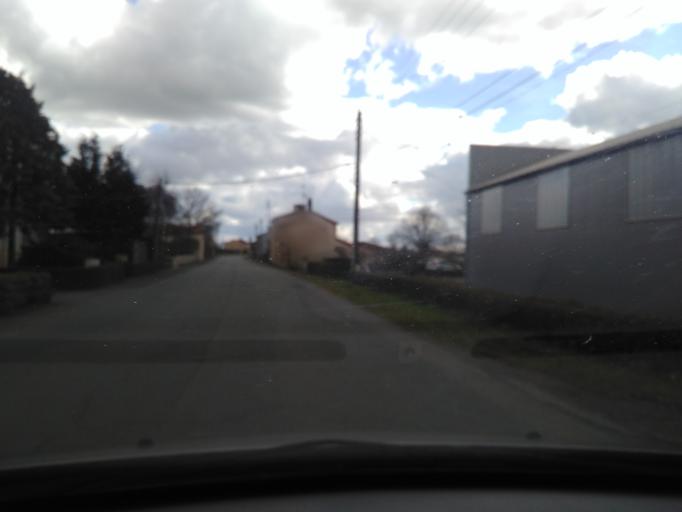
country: FR
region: Pays de la Loire
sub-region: Departement de la Vendee
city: Saint-Martin-des-Noyers
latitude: 46.7292
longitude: -1.1814
